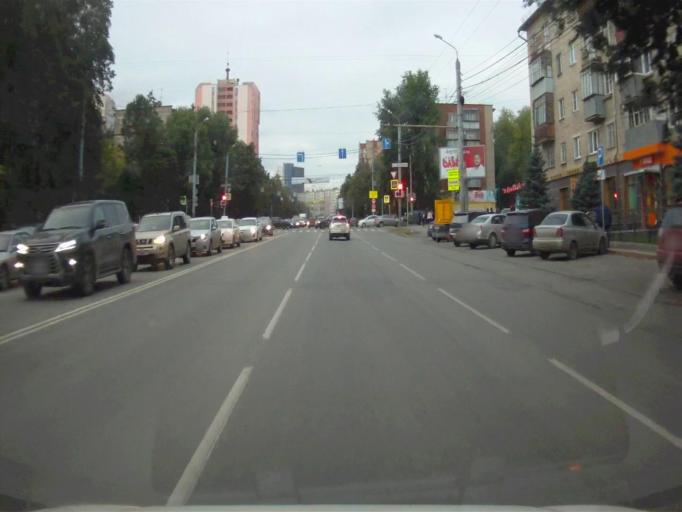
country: RU
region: Chelyabinsk
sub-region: Gorod Chelyabinsk
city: Chelyabinsk
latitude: 55.1589
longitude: 61.3809
